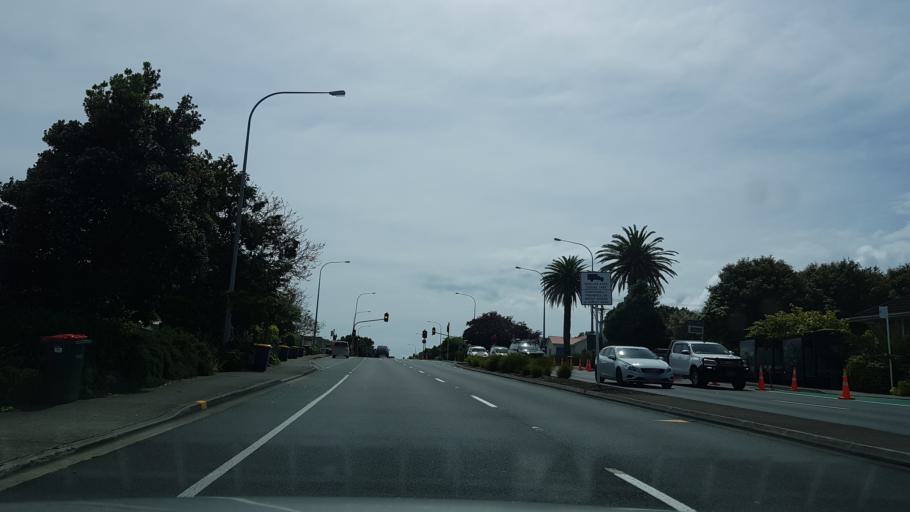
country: NZ
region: Auckland
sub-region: Auckland
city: North Shore
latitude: -36.7951
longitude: 174.7720
